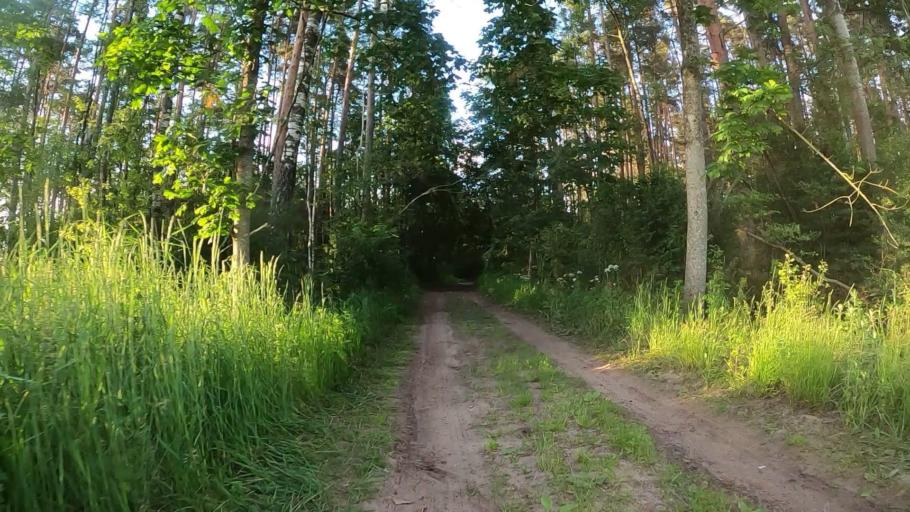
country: LV
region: Marupe
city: Marupe
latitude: 56.8766
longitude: 24.0038
